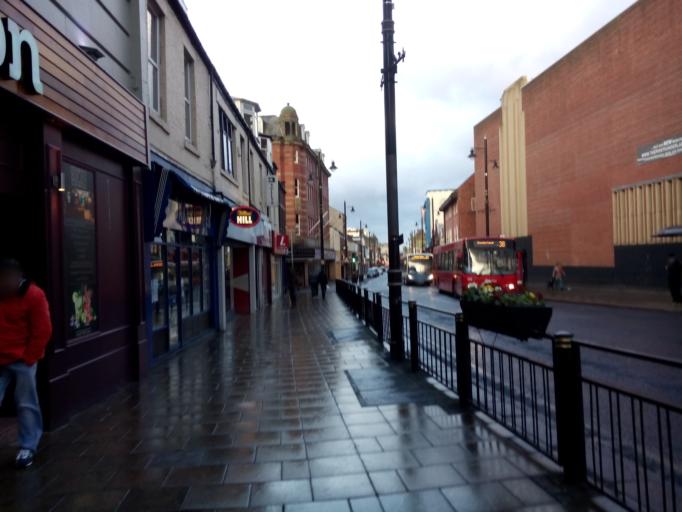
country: GB
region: England
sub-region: Sunderland
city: Sunderland
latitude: 54.9042
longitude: -1.3860
